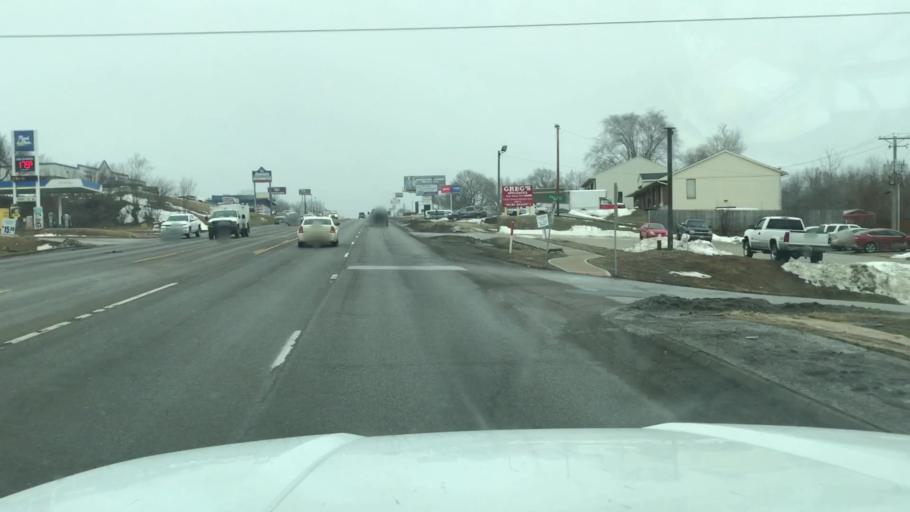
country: US
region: Missouri
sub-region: Buchanan County
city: Saint Joseph
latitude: 39.7478
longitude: -94.8023
